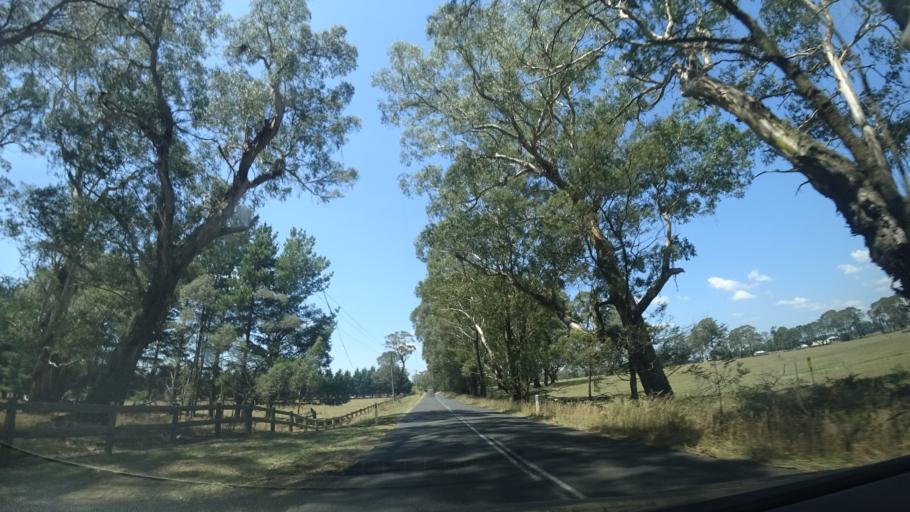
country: AU
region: New South Wales
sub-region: Wingecarribee
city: Bundanoon
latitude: -34.6095
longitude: 150.2765
